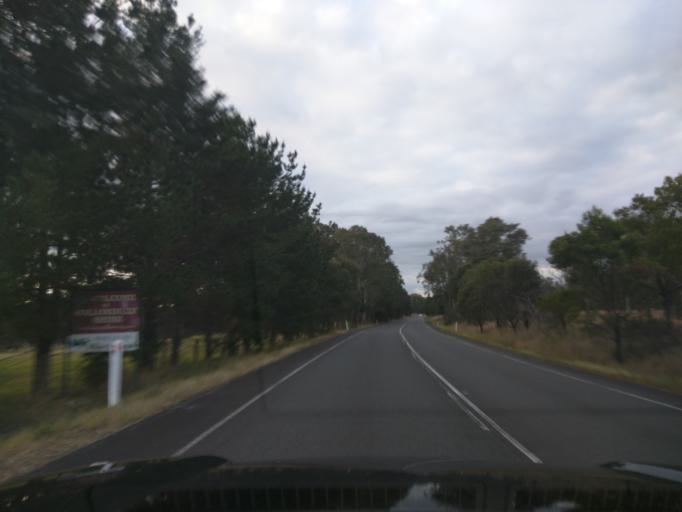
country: AU
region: New South Wales
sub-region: Wollondilly
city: Douglas Park
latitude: -34.2576
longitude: 150.7217
